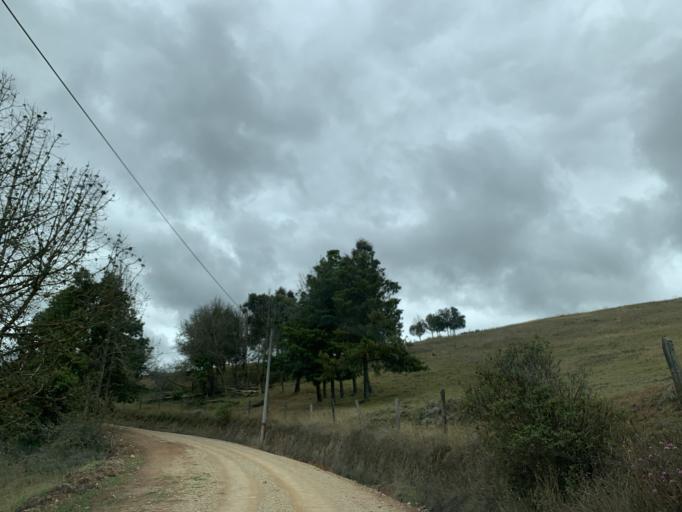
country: CO
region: Boyaca
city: Tunja
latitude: 5.5315
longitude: -73.3204
